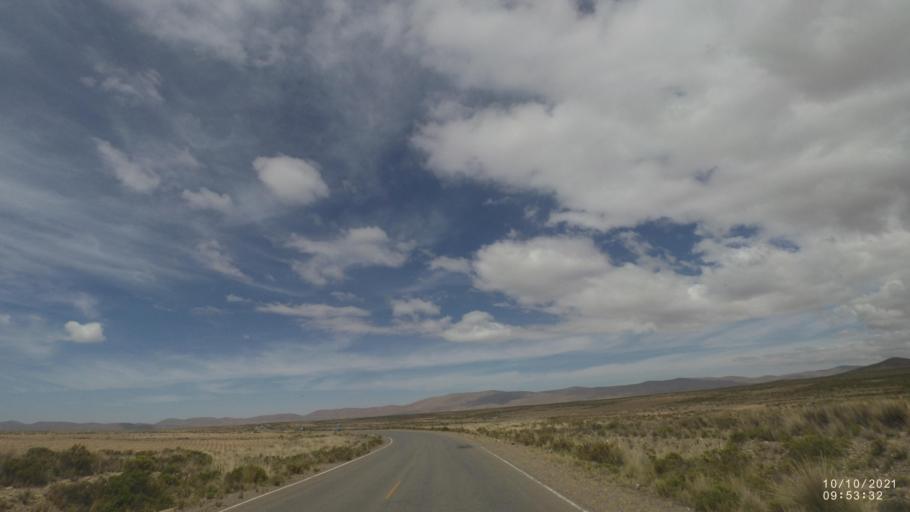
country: BO
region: La Paz
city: Colquiri
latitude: -17.2812
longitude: -67.3503
